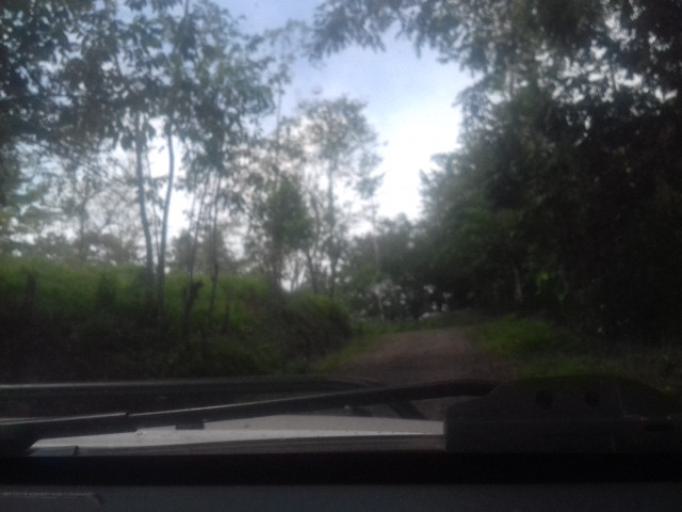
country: NI
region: Atlantico Norte (RAAN)
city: Waslala
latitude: 13.5022
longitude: -85.2339
